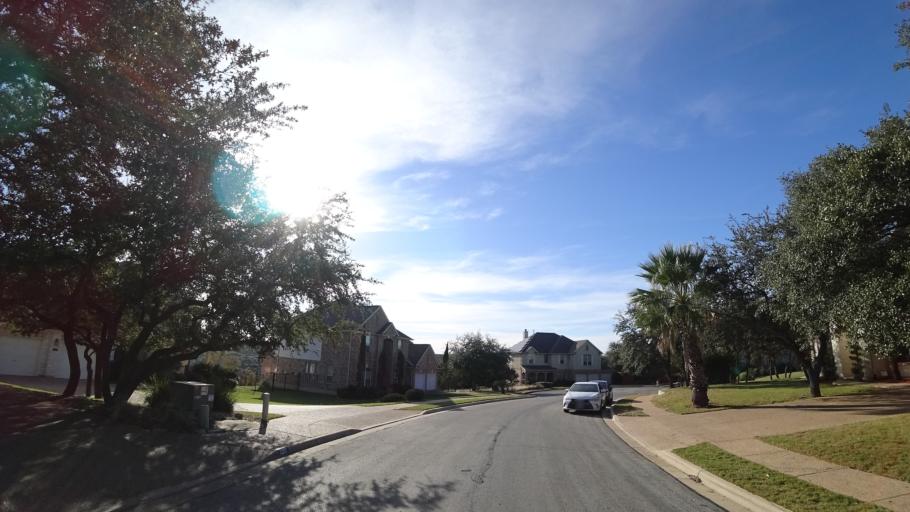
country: US
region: Texas
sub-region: Williamson County
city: Jollyville
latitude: 30.3999
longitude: -97.7759
